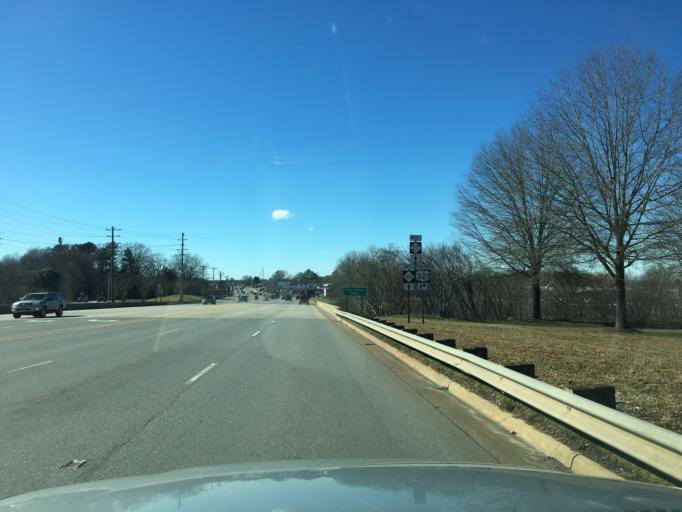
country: US
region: North Carolina
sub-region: Lincoln County
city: Lincolnton
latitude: 35.4782
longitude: -81.2286
